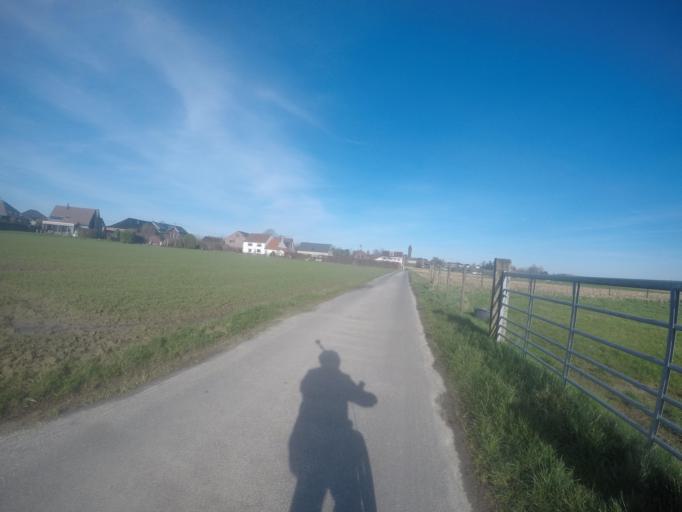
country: BE
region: Flanders
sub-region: Provincie Vlaams-Brabant
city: Pepingen
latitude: 50.7309
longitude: 4.1061
